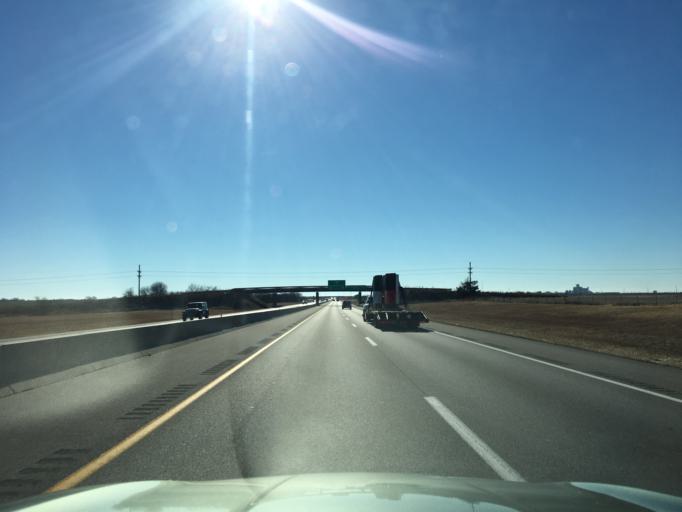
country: US
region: Kansas
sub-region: Sumner County
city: Wellington
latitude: 37.2925
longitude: -97.3403
